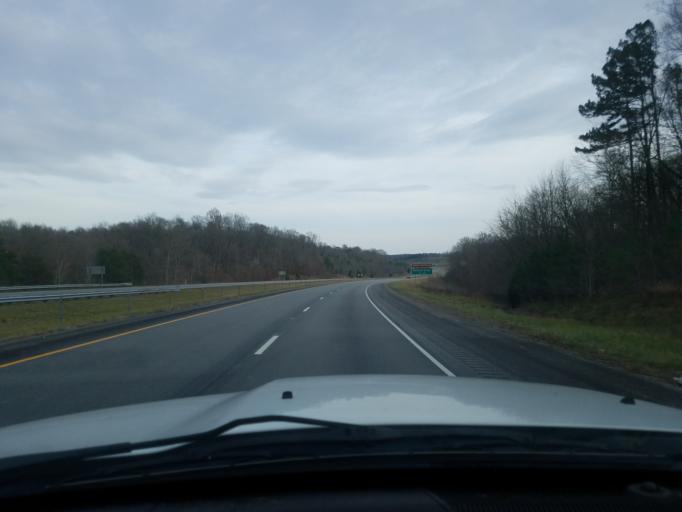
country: US
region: Indiana
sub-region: Crawford County
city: English
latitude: 38.2296
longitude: -86.6066
